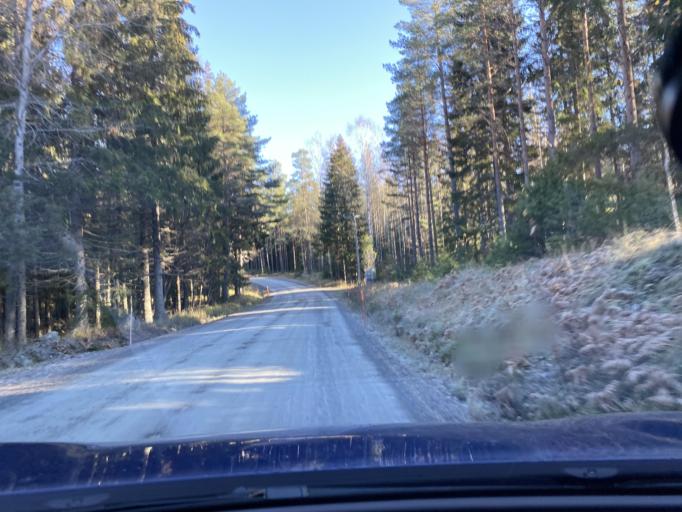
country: FI
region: Haeme
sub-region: Haemeenlinna
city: Kalvola
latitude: 60.9954
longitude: 24.1001
